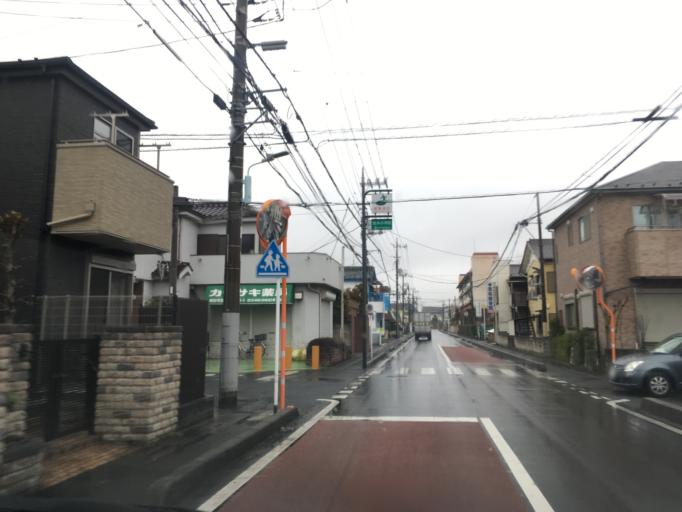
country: JP
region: Saitama
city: Koshigaya
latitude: 35.8888
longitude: 139.7793
